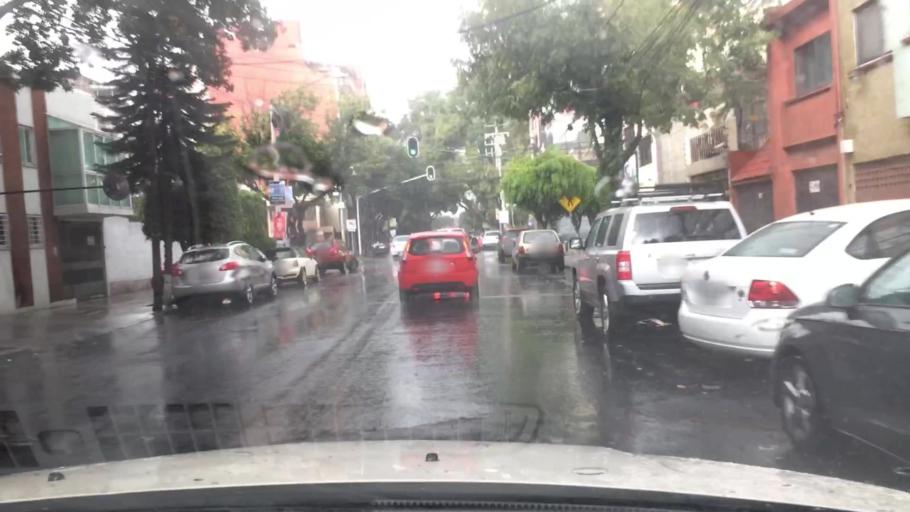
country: MX
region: Mexico City
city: Colonia del Valle
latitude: 19.3699
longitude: -99.1748
